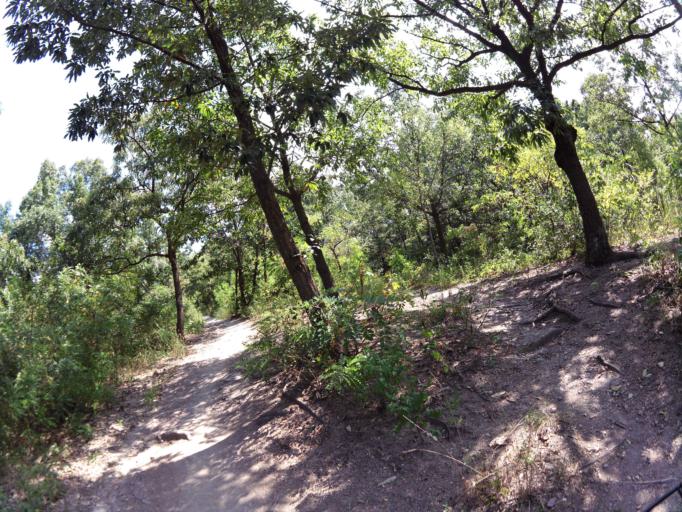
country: KR
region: Daegu
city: Daegu
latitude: 35.8588
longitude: 128.6508
